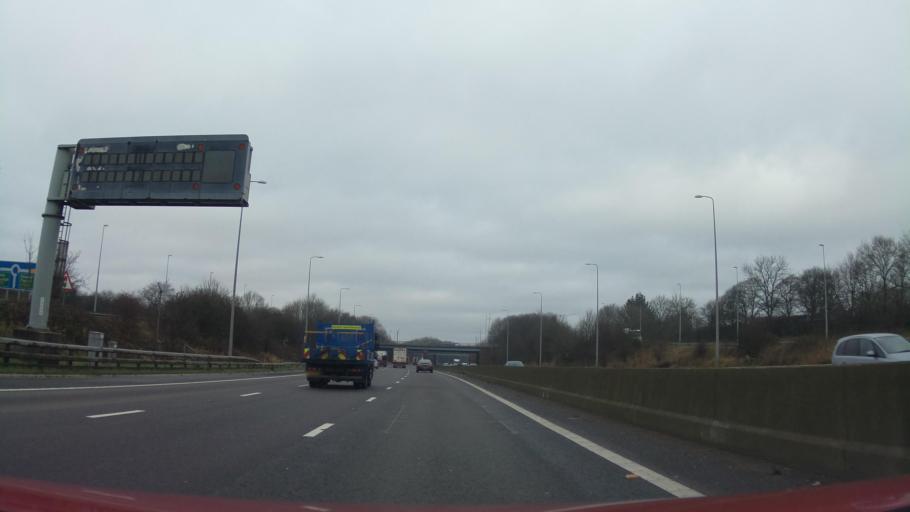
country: GB
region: England
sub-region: Borough of Wigan
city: Shevington
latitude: 53.5869
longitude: -2.6940
